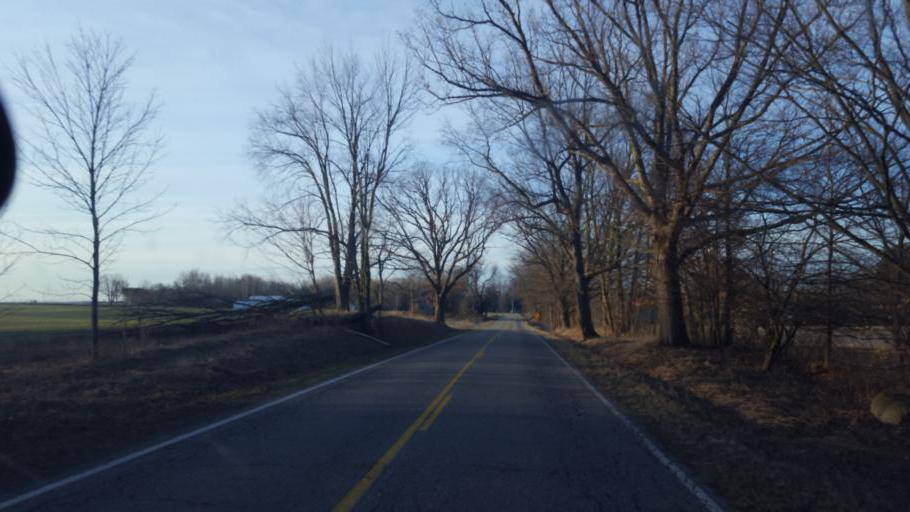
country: US
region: Michigan
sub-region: Montcalm County
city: Edmore
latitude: 43.4694
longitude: -85.0449
